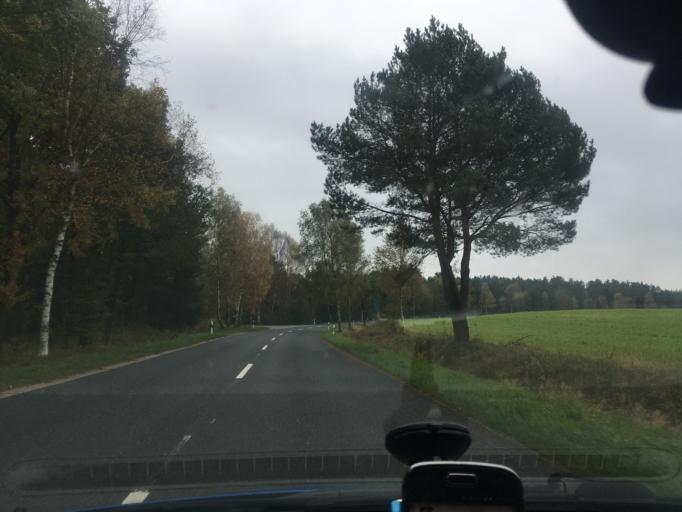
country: DE
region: Lower Saxony
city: Soderstorf
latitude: 53.1096
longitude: 10.0800
